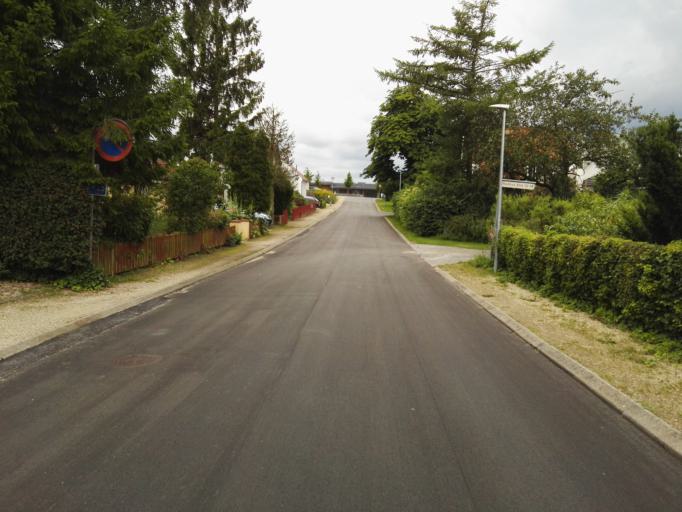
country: DK
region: Capital Region
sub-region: Egedal Kommune
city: Olstykke
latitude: 55.7933
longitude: 12.1590
